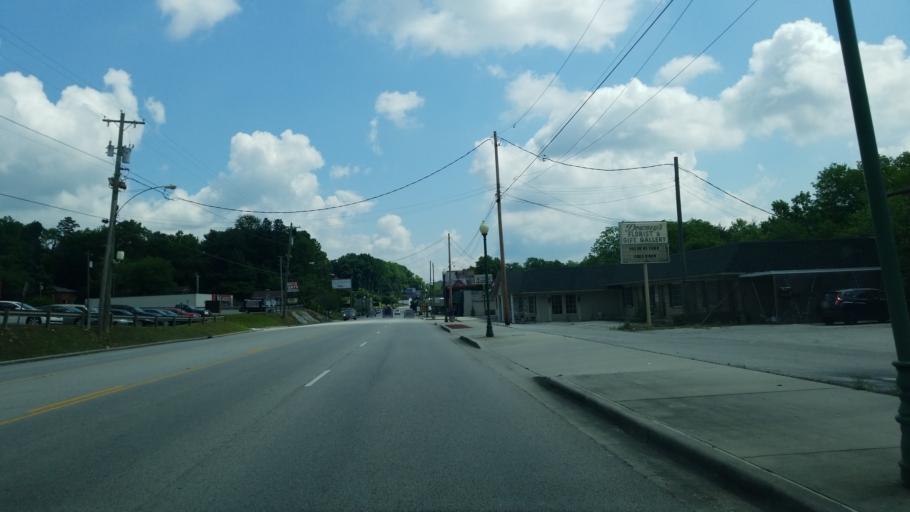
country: US
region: Tennessee
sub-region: Hamilton County
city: Red Bank
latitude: 35.0917
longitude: -85.3102
